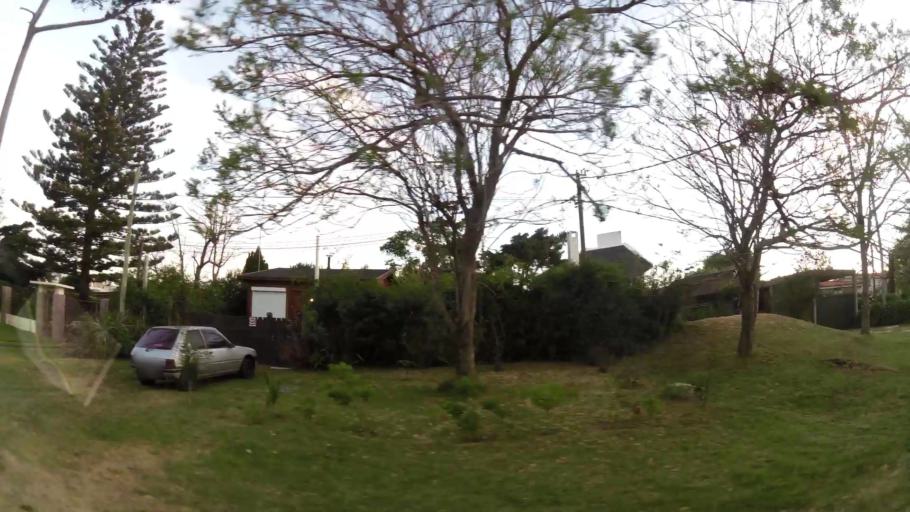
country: UY
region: Canelones
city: Atlantida
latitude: -34.7781
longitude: -55.7498
